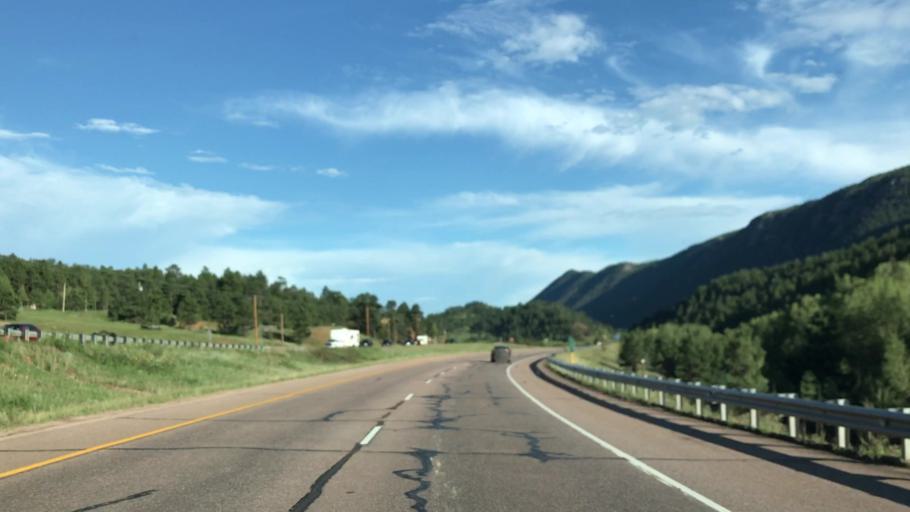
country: US
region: Colorado
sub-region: El Paso County
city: Cascade-Chipita Park
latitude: 38.9471
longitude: -105.0222
